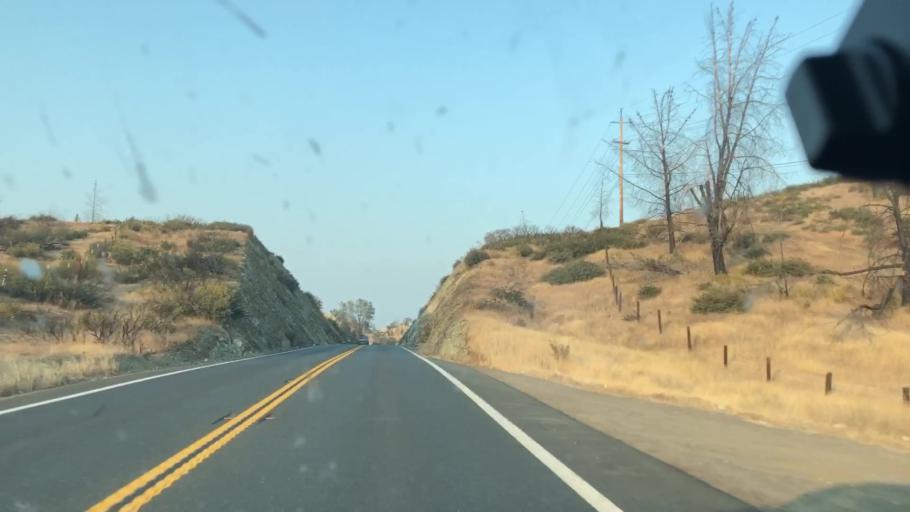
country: US
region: California
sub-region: Lake County
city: Middletown
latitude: 38.7643
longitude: -122.5965
